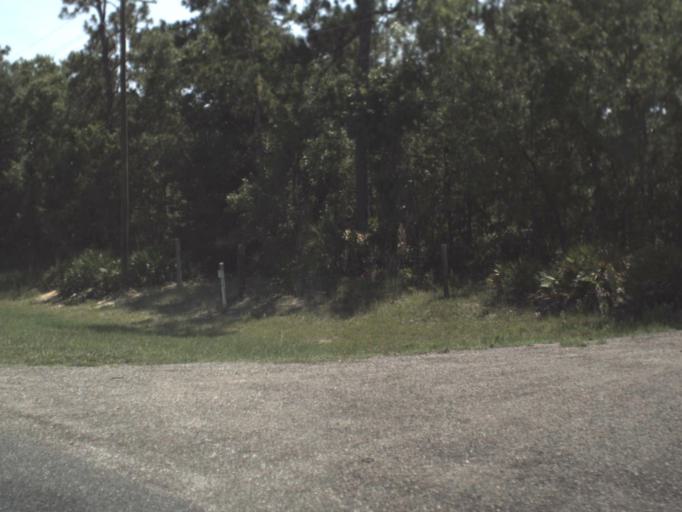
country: US
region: Florida
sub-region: Levy County
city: Inglis
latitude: 29.1227
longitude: -82.6368
